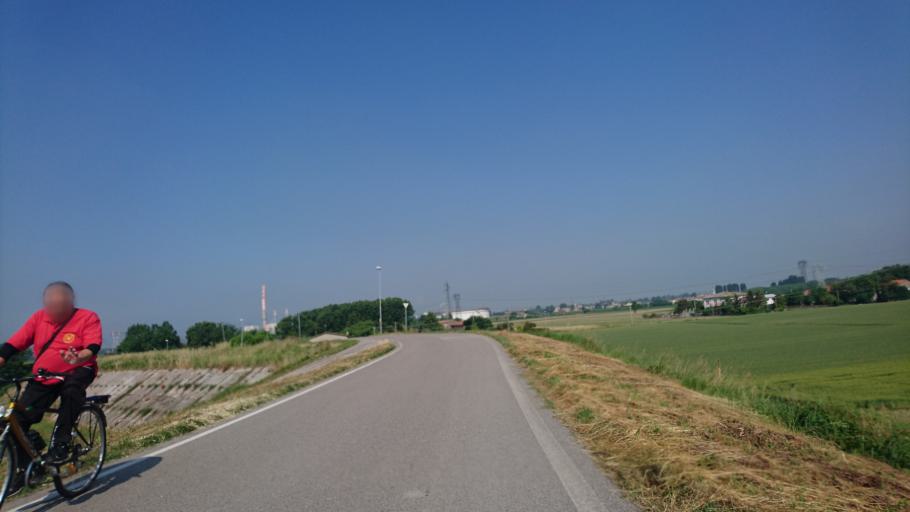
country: IT
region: Lombardy
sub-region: Provincia di Mantova
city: Ostiglia
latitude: 45.0578
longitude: 11.1646
